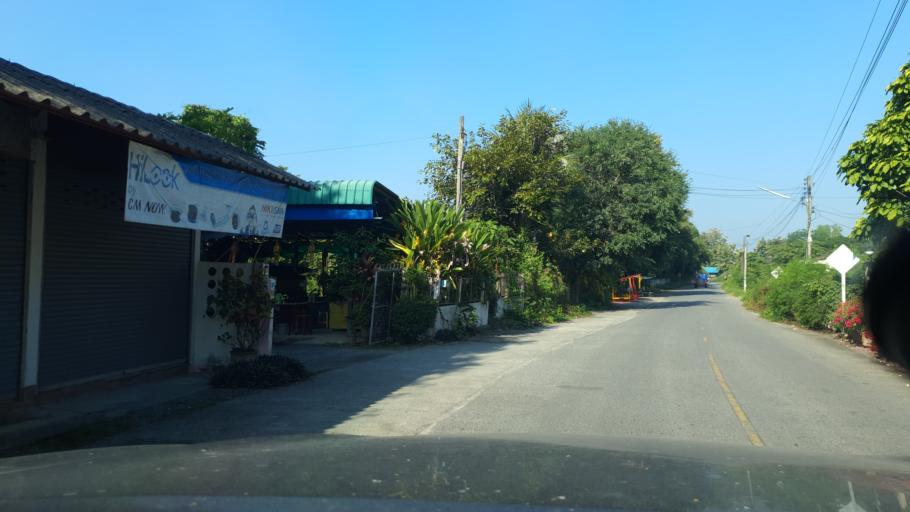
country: TH
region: Chiang Mai
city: San Kamphaeng
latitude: 18.7529
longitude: 99.1418
